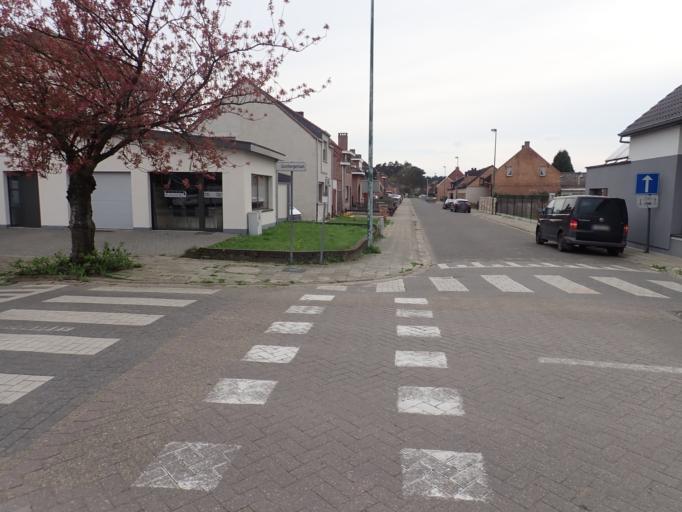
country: BE
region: Flanders
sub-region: Provincie Antwerpen
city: Vorselaar
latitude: 51.2028
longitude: 4.7656
